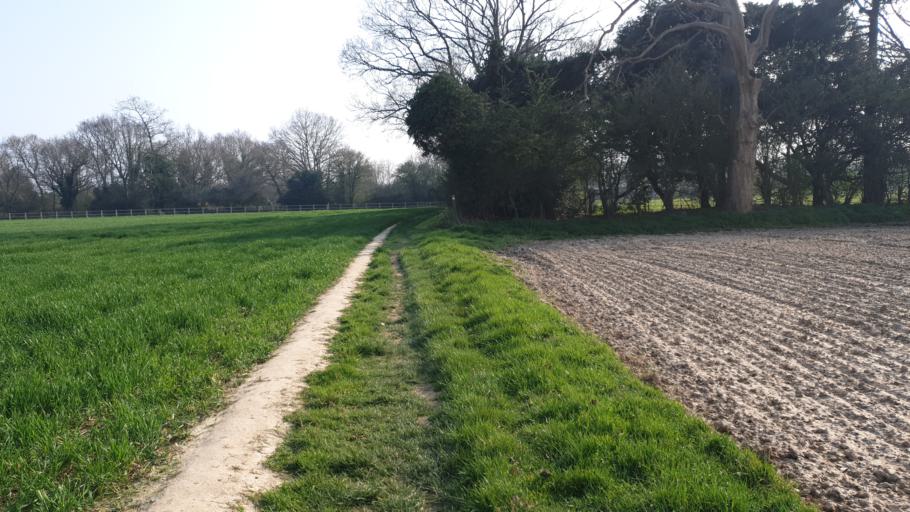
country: GB
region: England
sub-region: Essex
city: Little Clacton
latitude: 51.8773
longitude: 1.1179
